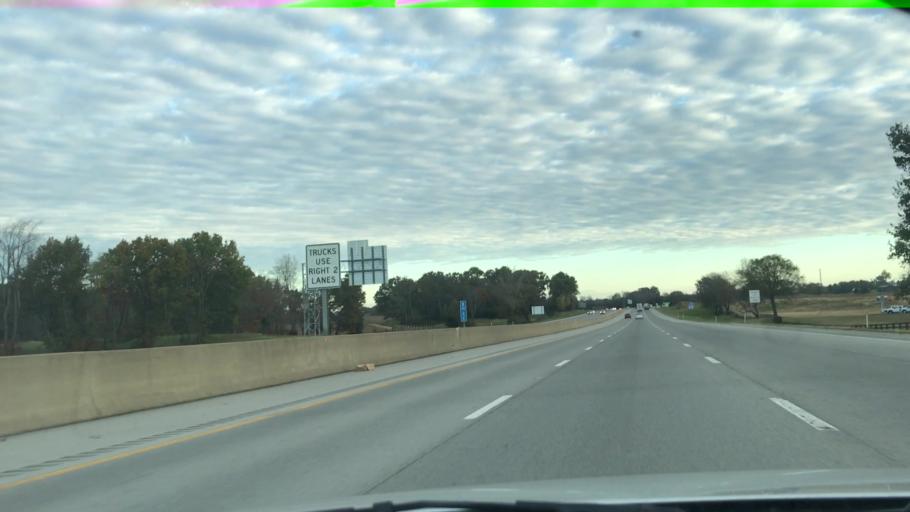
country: US
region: Kentucky
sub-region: Simpson County
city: Franklin
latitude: 36.7230
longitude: -86.5181
